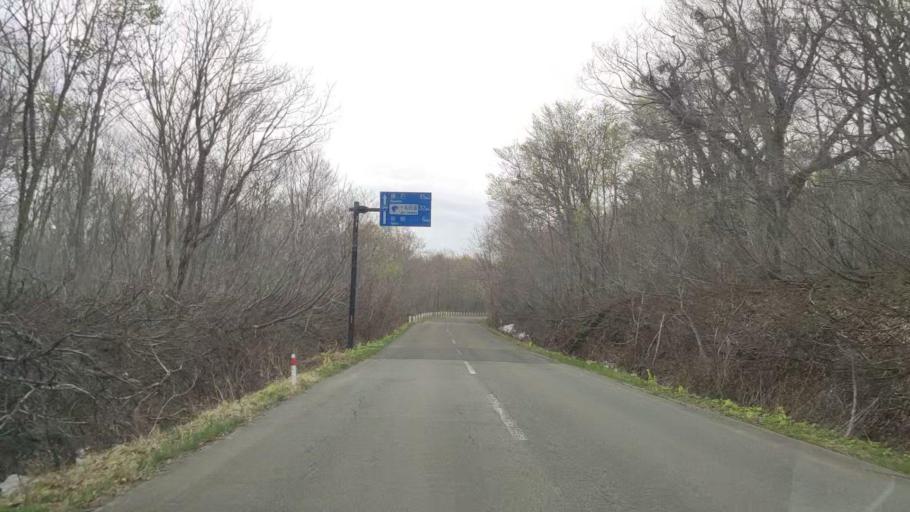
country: JP
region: Aomori
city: Aomori Shi
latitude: 40.6629
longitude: 140.9597
